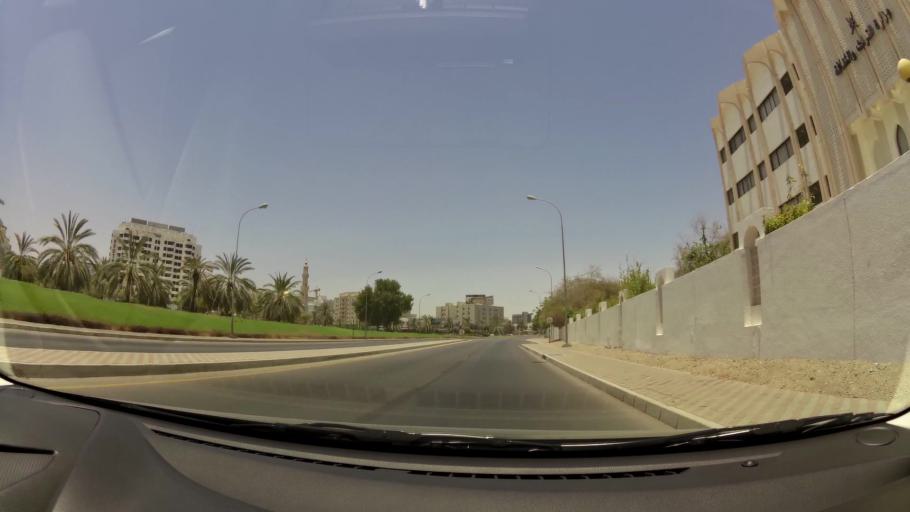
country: OM
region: Muhafazat Masqat
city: Bawshar
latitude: 23.5985
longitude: 58.4234
